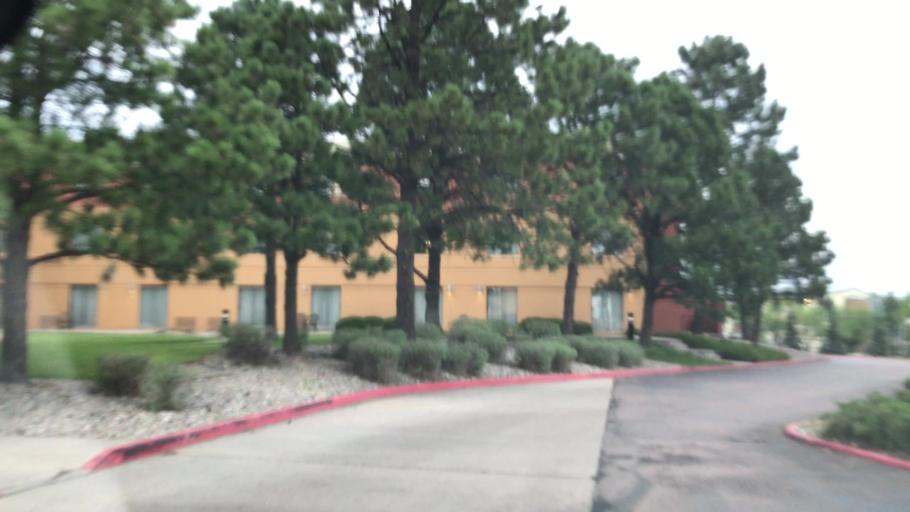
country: US
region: Colorado
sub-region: El Paso County
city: Stratmoor
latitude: 38.7990
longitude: -104.7955
